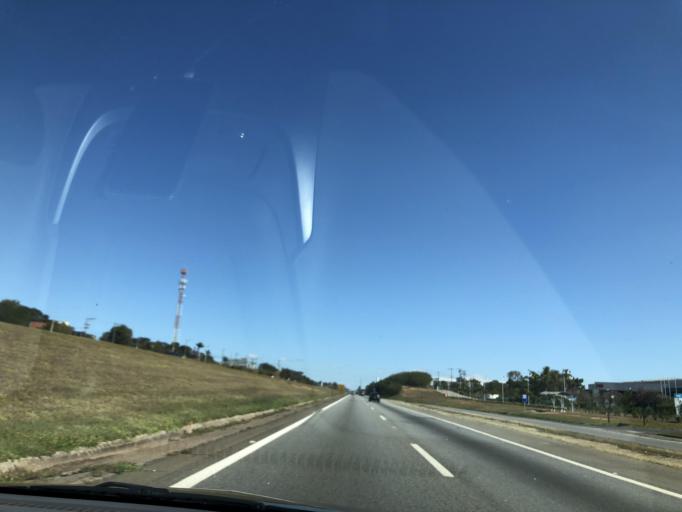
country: BR
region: Sao Paulo
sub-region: Sorocaba
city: Sorocaba
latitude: -23.4263
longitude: -47.3609
